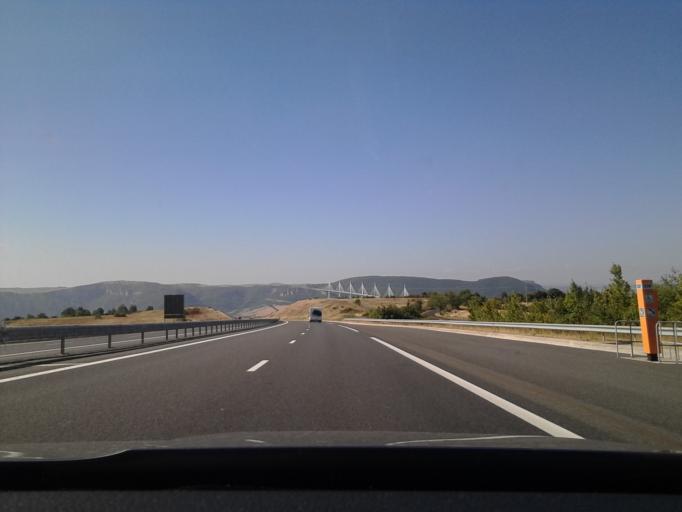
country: FR
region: Midi-Pyrenees
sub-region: Departement de l'Aveyron
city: Creissels
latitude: 44.1195
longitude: 3.0292
